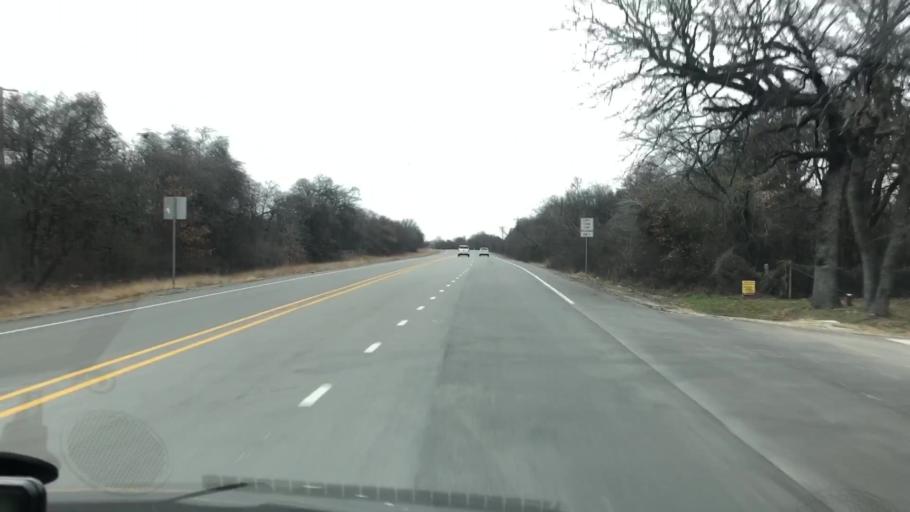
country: US
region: Texas
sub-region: Hamilton County
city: Hico
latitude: 32.0921
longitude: -98.1052
